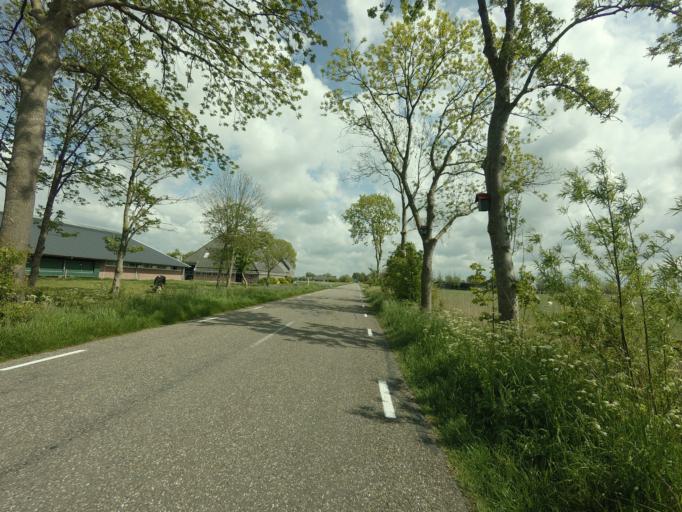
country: NL
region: Friesland
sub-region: Gemeente Littenseradiel
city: Makkum
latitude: 53.0978
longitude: 5.6519
